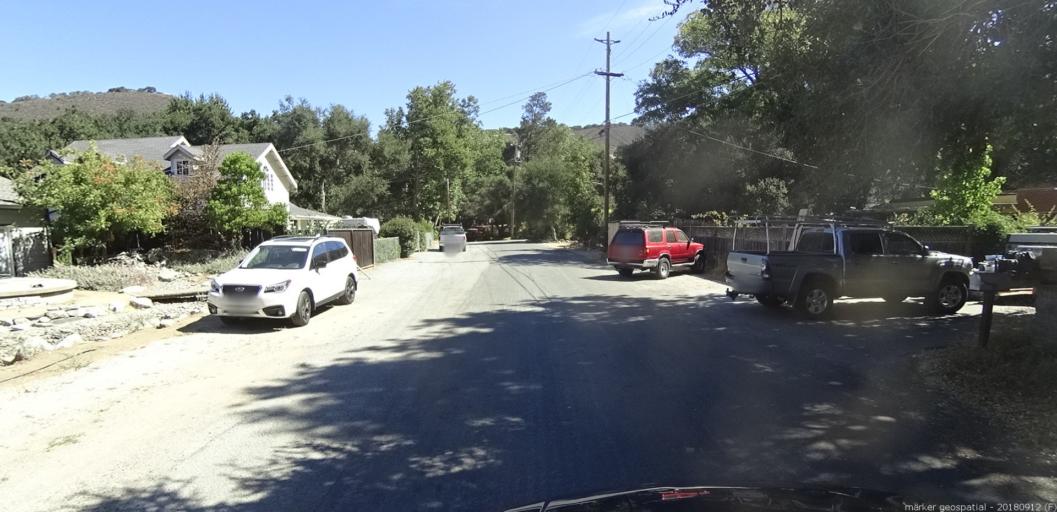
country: US
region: California
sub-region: Monterey County
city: Carmel Valley Village
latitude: 36.4741
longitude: -121.7217
